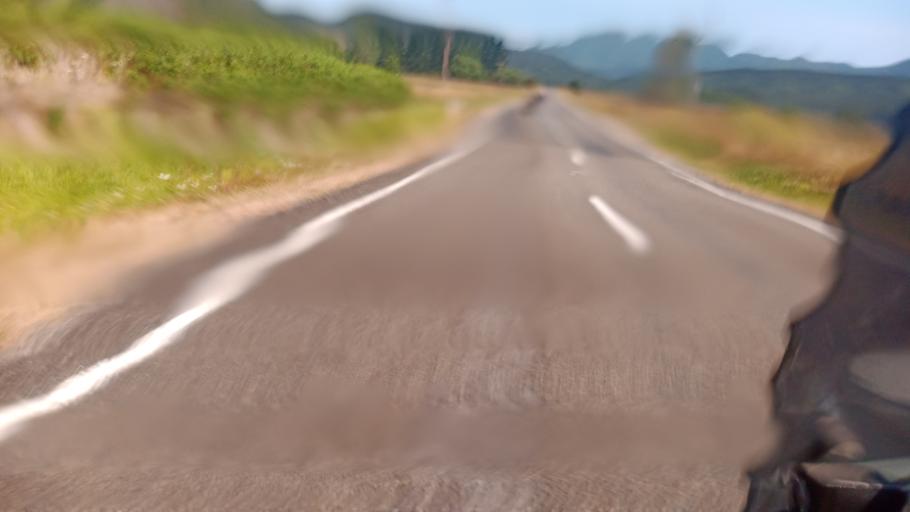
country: NZ
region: Bay of Plenty
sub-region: Opotiki District
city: Opotiki
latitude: -37.5937
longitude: 178.2570
